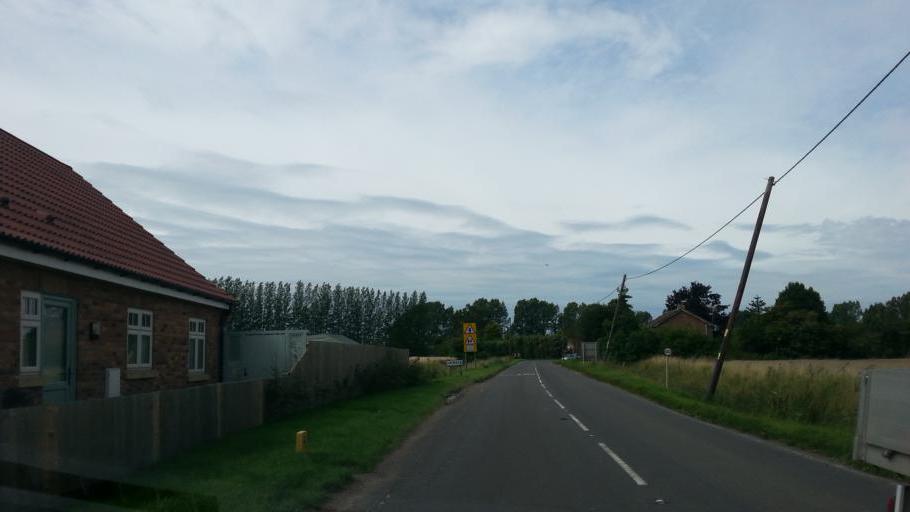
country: GB
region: England
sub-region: Norfolk
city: Outwell
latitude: 52.5817
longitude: 0.2189
